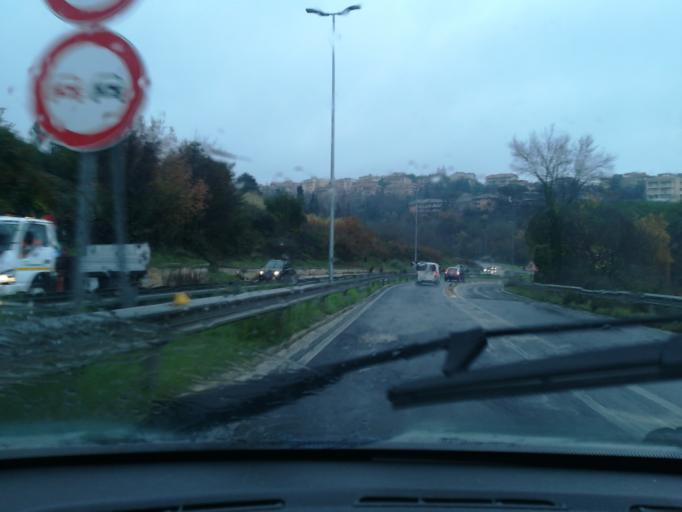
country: IT
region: The Marches
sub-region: Provincia di Macerata
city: Macerata
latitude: 43.2904
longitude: 13.4414
